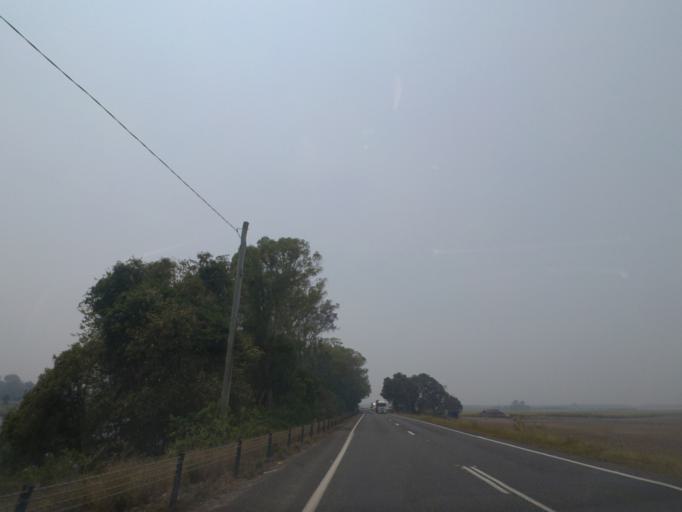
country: AU
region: New South Wales
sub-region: Clarence Valley
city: Maclean
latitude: -29.5412
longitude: 153.1636
